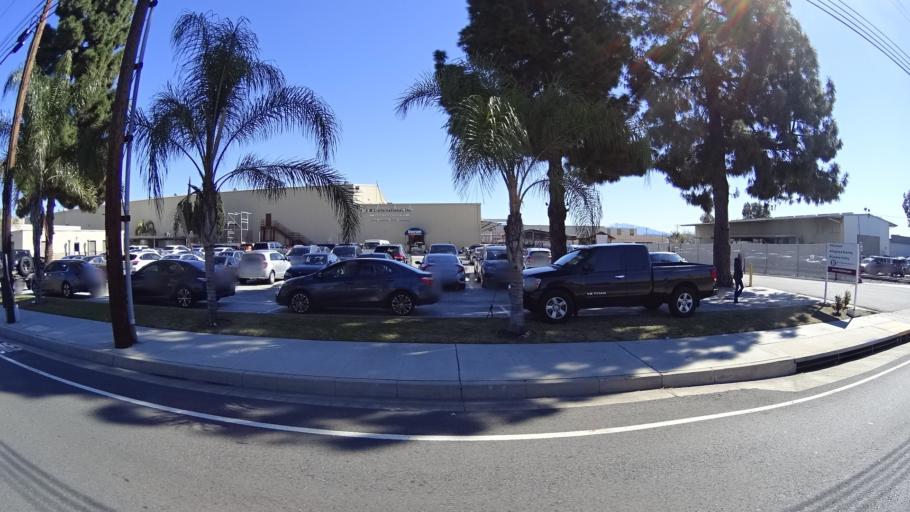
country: US
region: California
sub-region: Orange County
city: Orange
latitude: 33.8220
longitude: -117.8620
